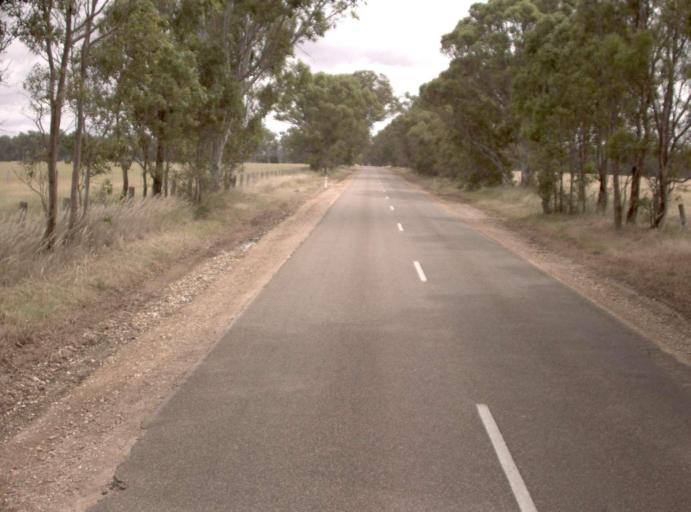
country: AU
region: Victoria
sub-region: Wellington
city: Sale
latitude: -37.8756
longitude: 147.0663
